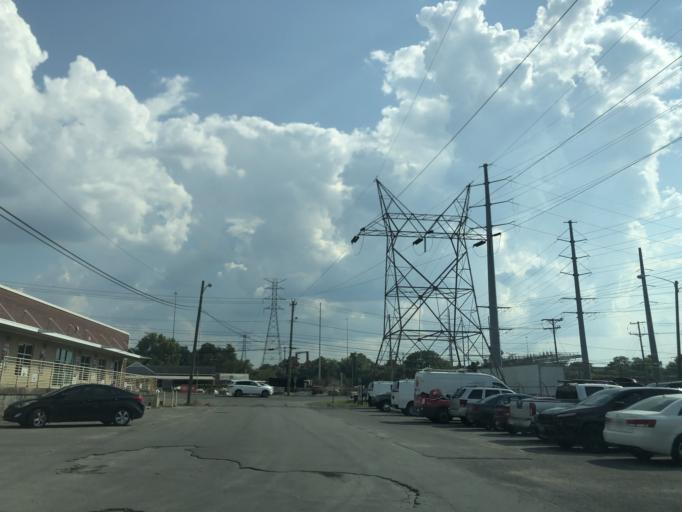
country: US
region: Tennessee
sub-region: Davidson County
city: Oak Hill
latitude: 36.1204
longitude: -86.7705
